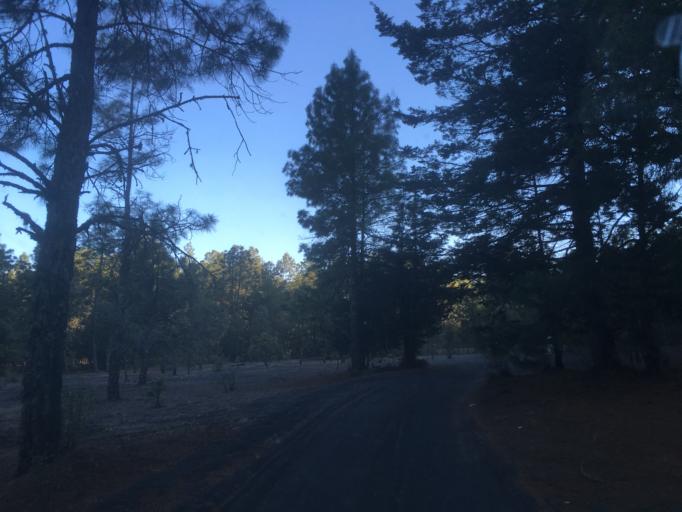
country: MX
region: Michoacan
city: Angahuan
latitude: 19.4668
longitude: -102.2400
